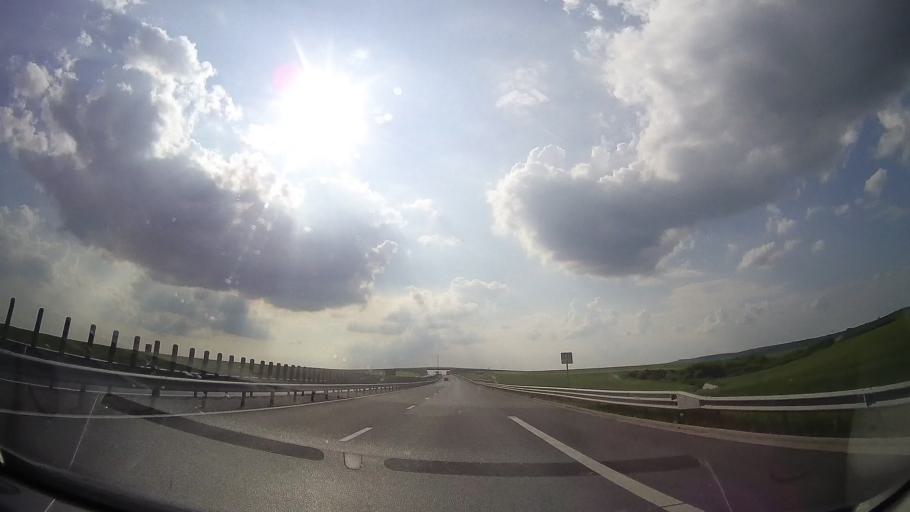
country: RO
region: Timis
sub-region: Comuna Ghizela
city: Ghizela
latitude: 45.7983
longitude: 21.6809
